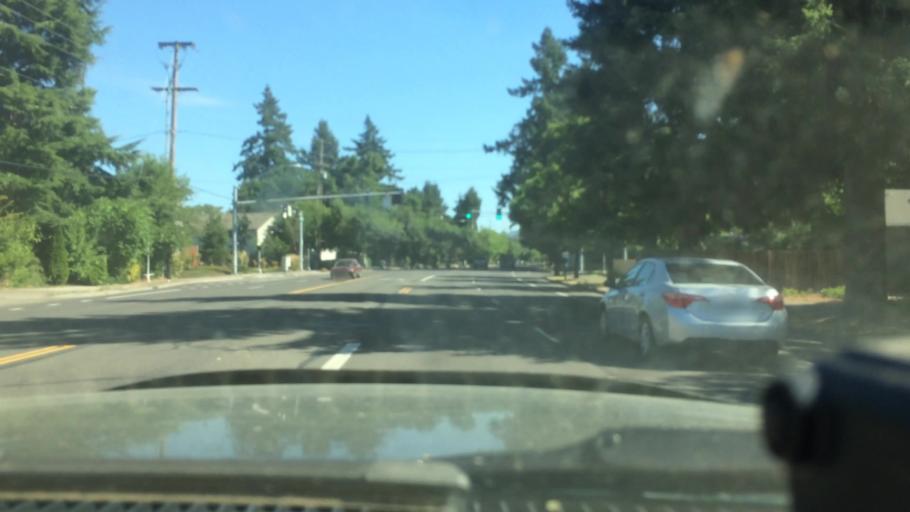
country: US
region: Oregon
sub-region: Lane County
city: Eugene
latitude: 44.0753
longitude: -123.1195
